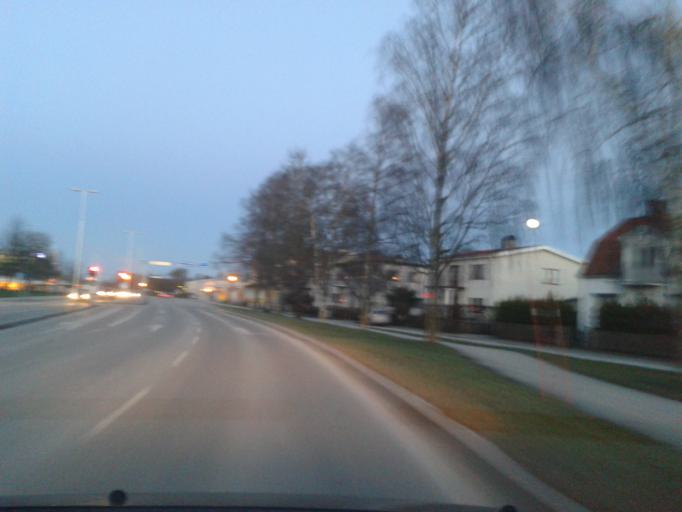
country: SE
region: Gotland
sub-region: Gotland
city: Visby
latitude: 57.6353
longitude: 18.3016
